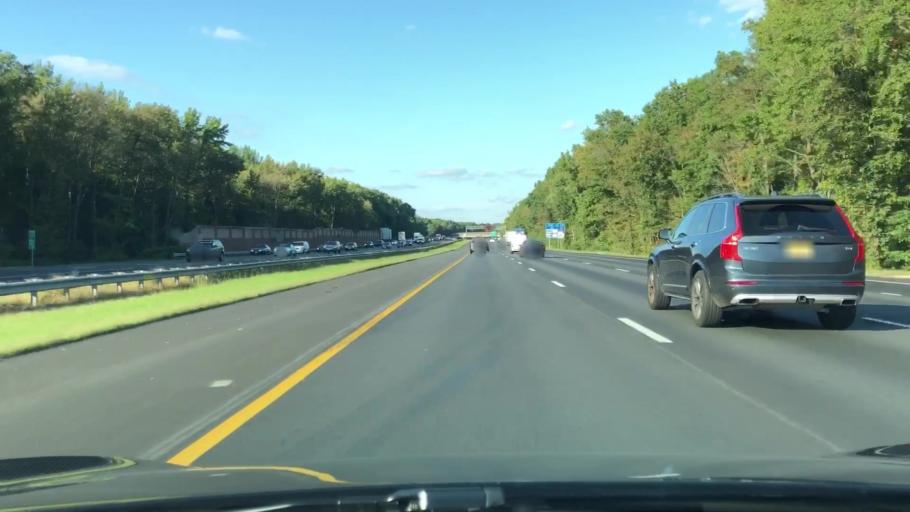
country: US
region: New Jersey
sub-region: Camden County
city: Kingston Estates
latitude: 39.9140
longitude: -74.9819
